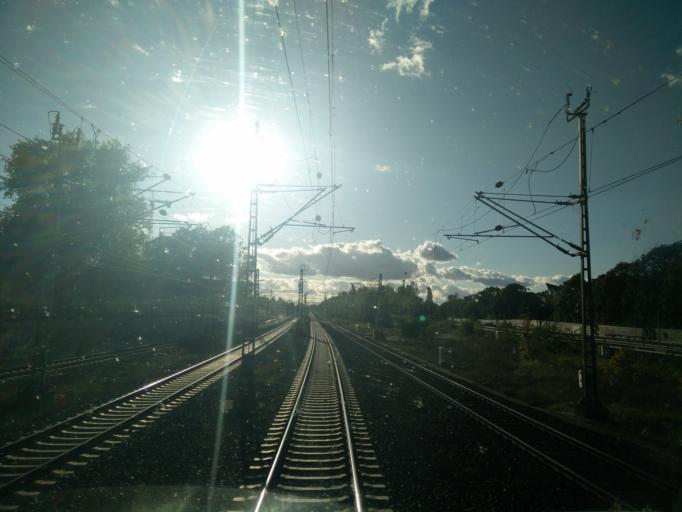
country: DE
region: Berlin
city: Halensee
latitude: 52.5034
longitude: 13.2984
